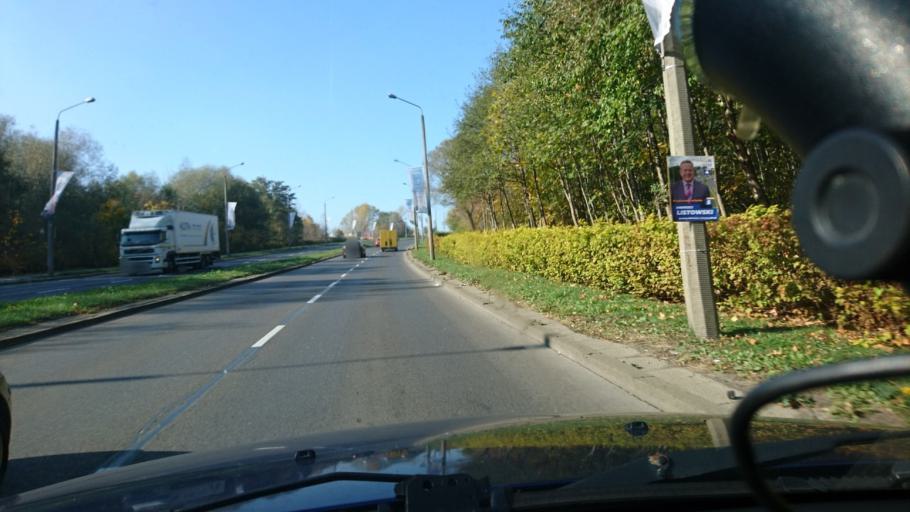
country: PL
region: Silesian Voivodeship
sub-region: Bielsko-Biala
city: Bielsko-Biala
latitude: 49.8006
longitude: 19.0373
